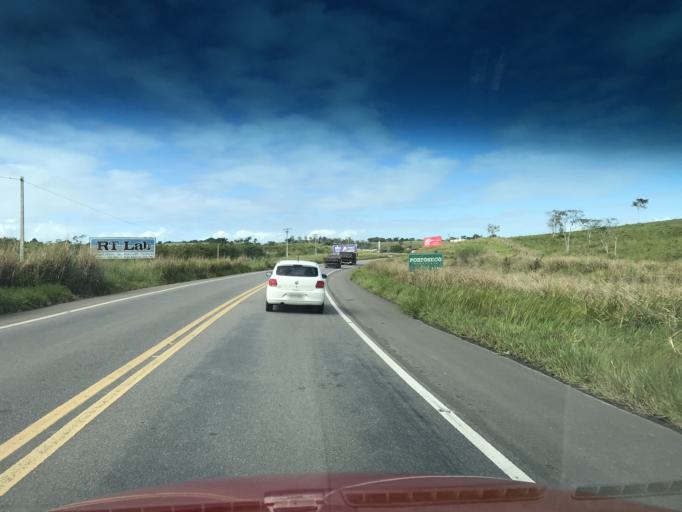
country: BR
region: Bahia
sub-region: Conceicao Do Almeida
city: Muritiba
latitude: -12.9402
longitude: -39.2513
